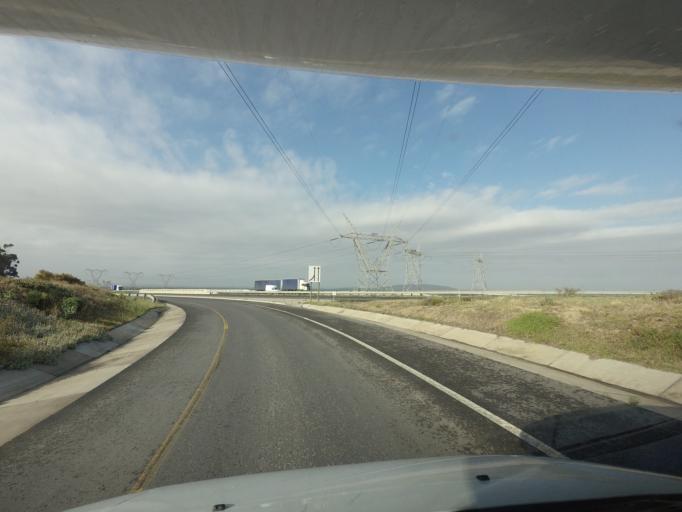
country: ZA
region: Western Cape
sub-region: City of Cape Town
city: Sunset Beach
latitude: -33.7246
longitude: 18.5448
